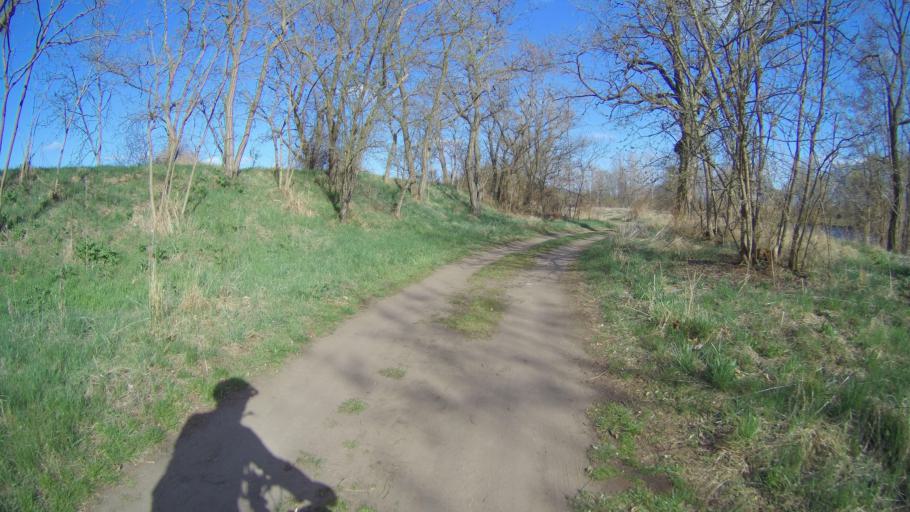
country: CZ
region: Ustecky
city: Zatec
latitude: 50.3549
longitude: 13.4841
